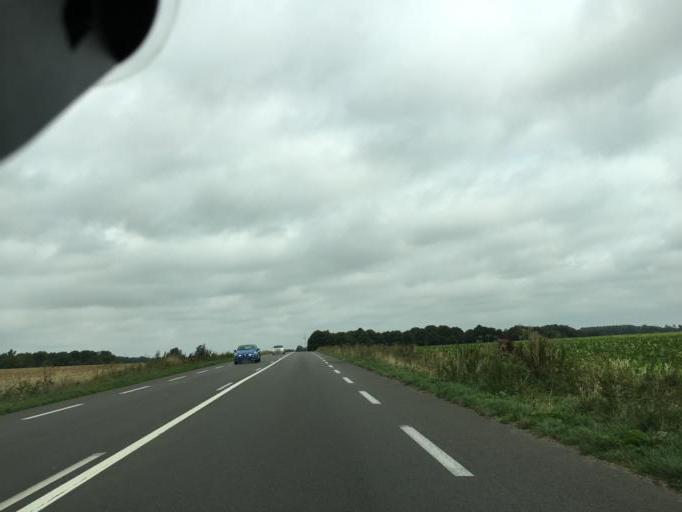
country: FR
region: Nord-Pas-de-Calais
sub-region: Departement du Pas-de-Calais
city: Saint-Pol-sur-Ternoise
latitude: 50.3969
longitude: 2.3573
